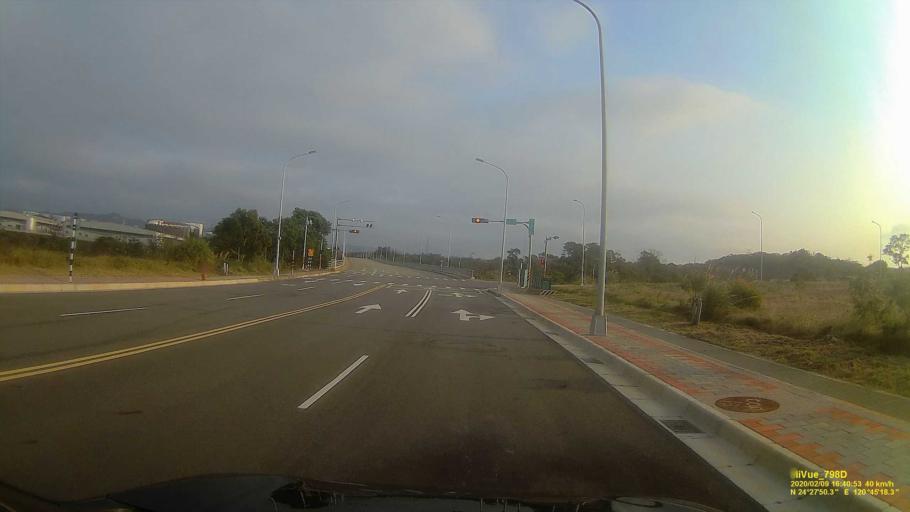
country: TW
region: Taiwan
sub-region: Miaoli
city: Miaoli
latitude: 24.4639
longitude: 120.7551
